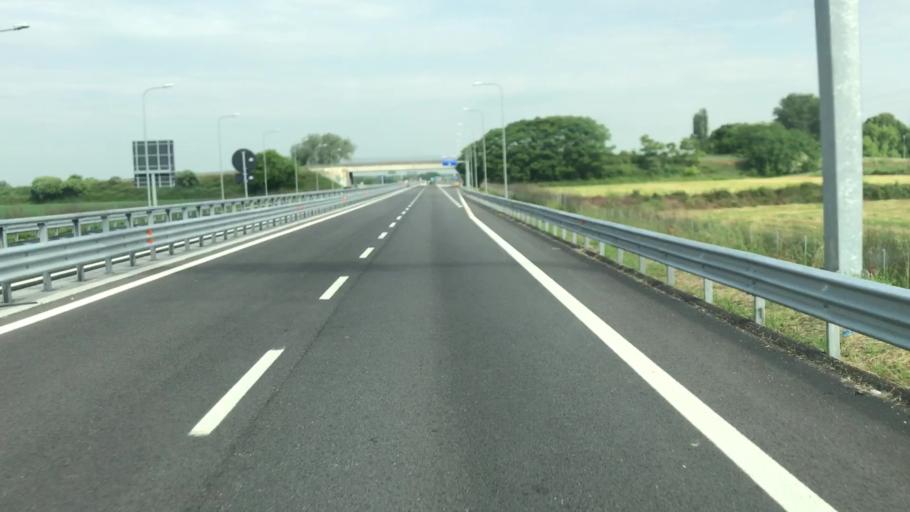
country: IT
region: Lombardy
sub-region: Provincia di Pavia
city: Torre d'Isola
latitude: 45.2196
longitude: 9.0851
